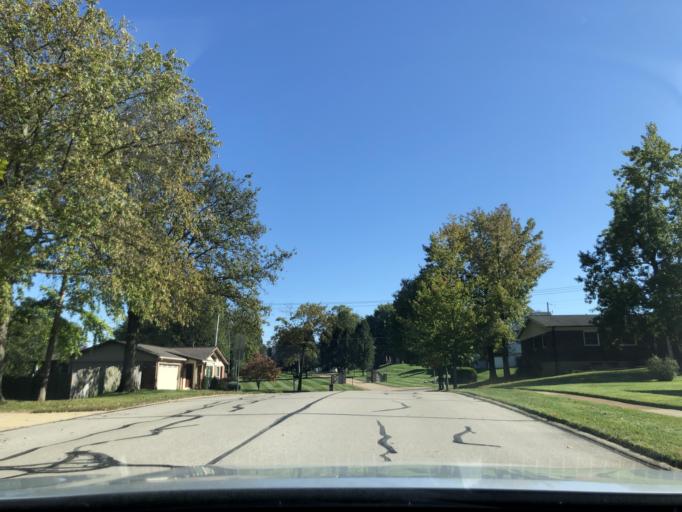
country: US
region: Missouri
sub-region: Saint Louis County
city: Concord
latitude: 38.4924
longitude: -90.3592
